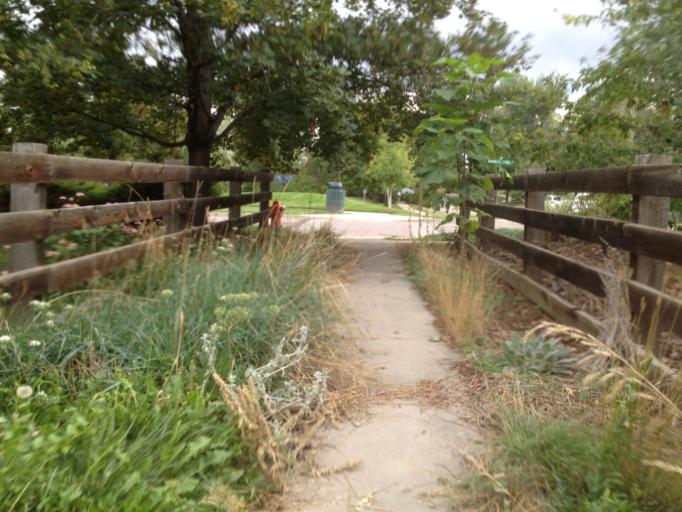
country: US
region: Colorado
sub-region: Boulder County
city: Louisville
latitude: 39.9805
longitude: -105.1391
